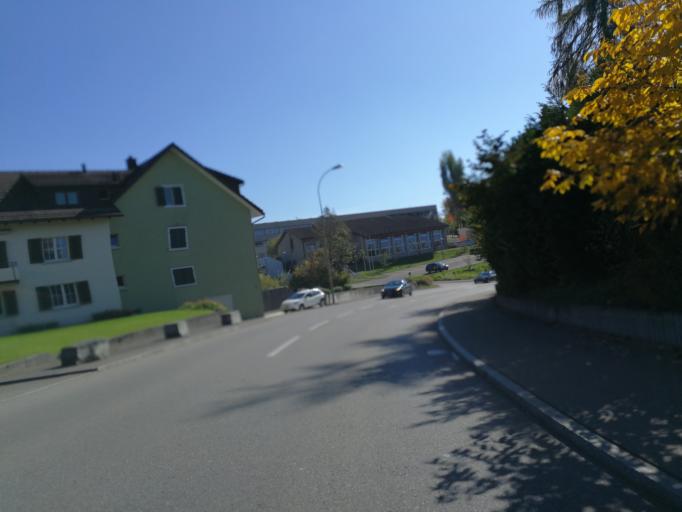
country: CH
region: Zurich
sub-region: Bezirk Meilen
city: Mannedorf
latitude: 47.2547
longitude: 8.7028
